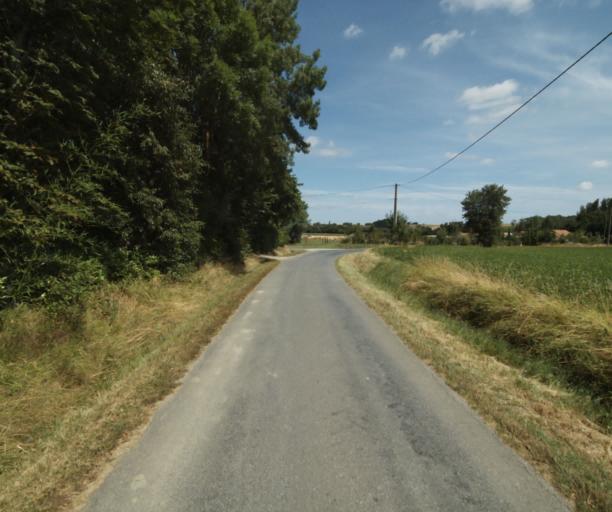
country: FR
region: Midi-Pyrenees
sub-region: Departement du Tarn
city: Soreze
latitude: 43.4970
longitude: 2.0829
